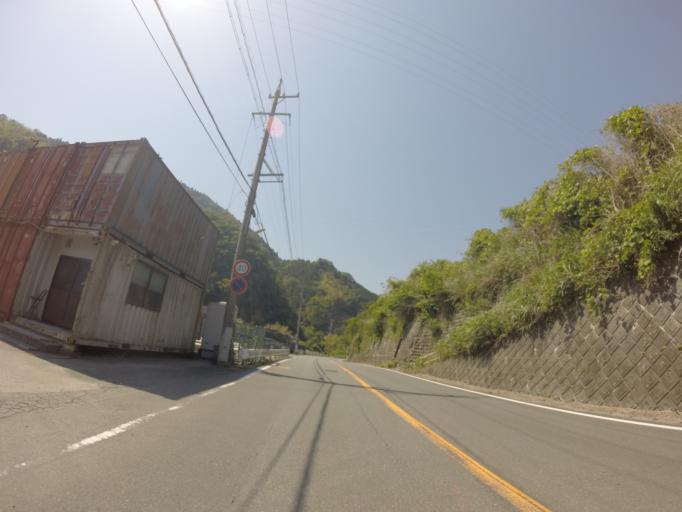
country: JP
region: Shizuoka
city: Fujinomiya
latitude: 35.1212
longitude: 138.5562
